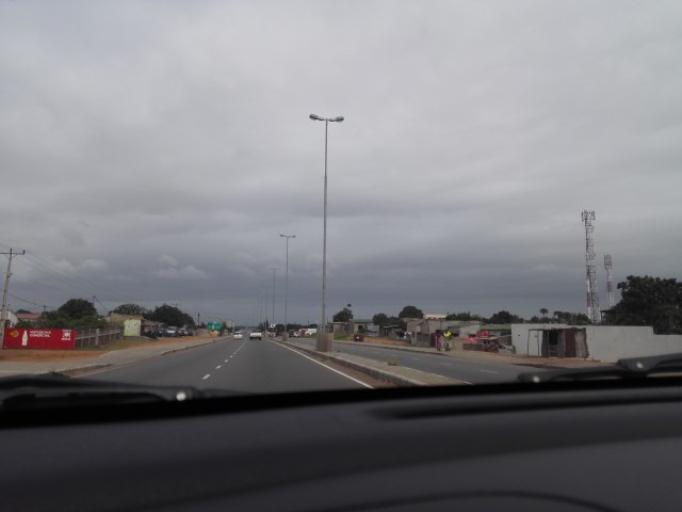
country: MZ
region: Maputo City
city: Maputo
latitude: -25.8227
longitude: 32.5898
